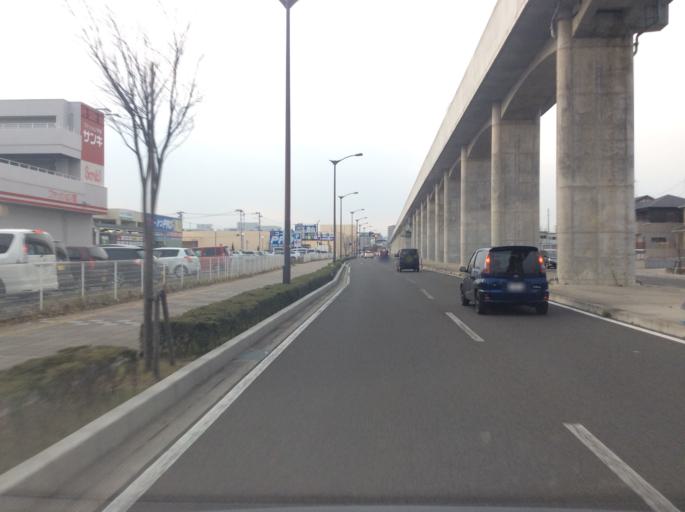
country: JP
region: Miyagi
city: Iwanuma
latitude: 38.1631
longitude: 140.9047
